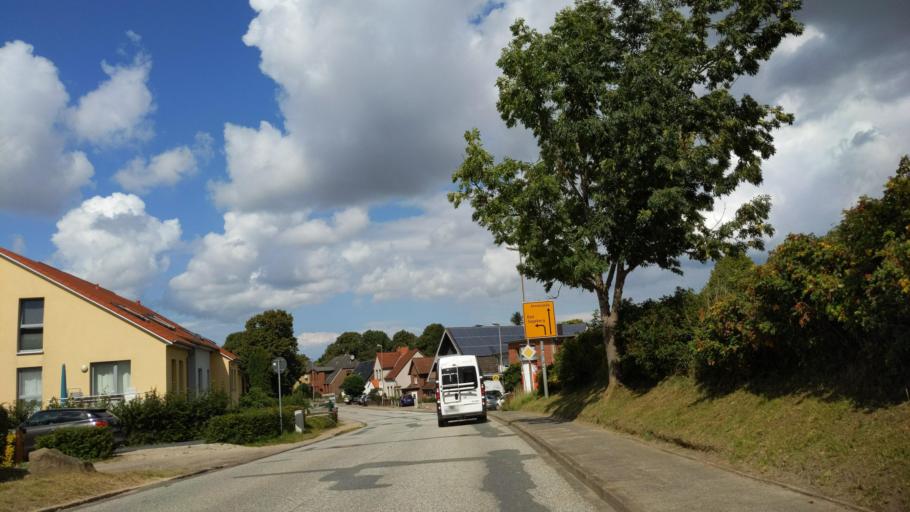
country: DE
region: Schleswig-Holstein
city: Reinfeld
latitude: 53.8284
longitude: 10.4775
